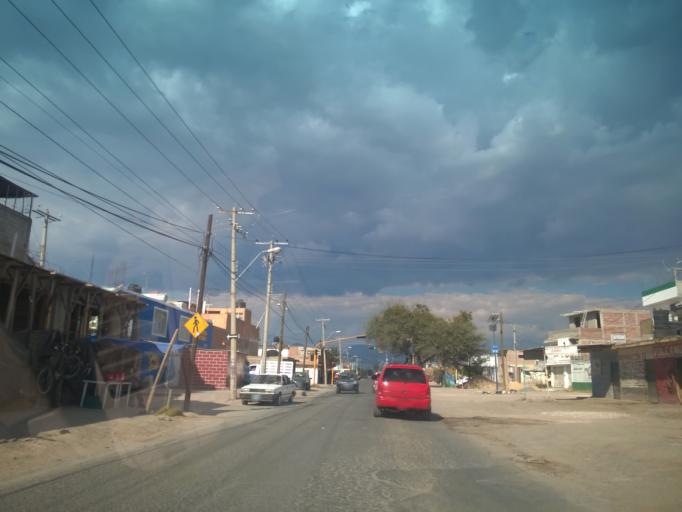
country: MX
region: Guanajuato
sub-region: Leon
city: San Jose de Duran (Los Troncoso)
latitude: 21.0668
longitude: -101.6244
